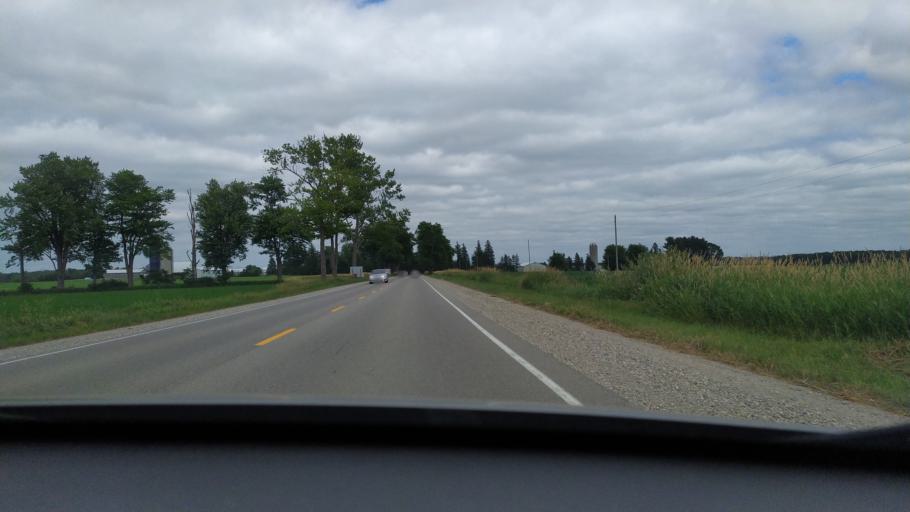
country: CA
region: Ontario
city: Stratford
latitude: 43.3160
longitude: -80.9699
